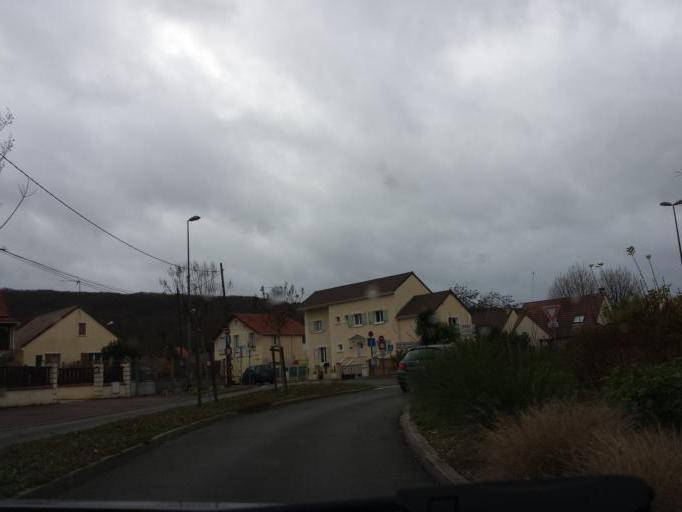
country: FR
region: Ile-de-France
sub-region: Departement du Val-d'Oise
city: Montigny-les-Cormeilles
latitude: 48.9893
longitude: 2.2127
